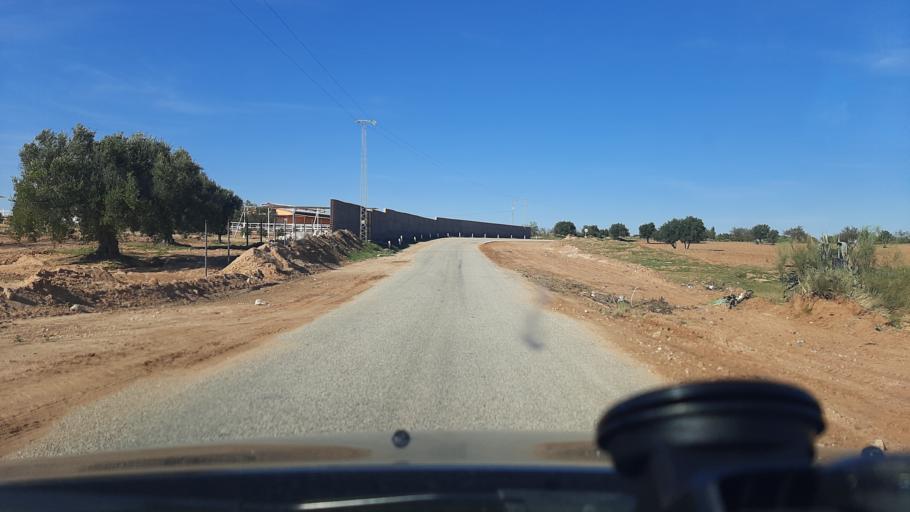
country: TN
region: Safaqis
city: Sfax
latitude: 34.9105
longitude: 10.5899
